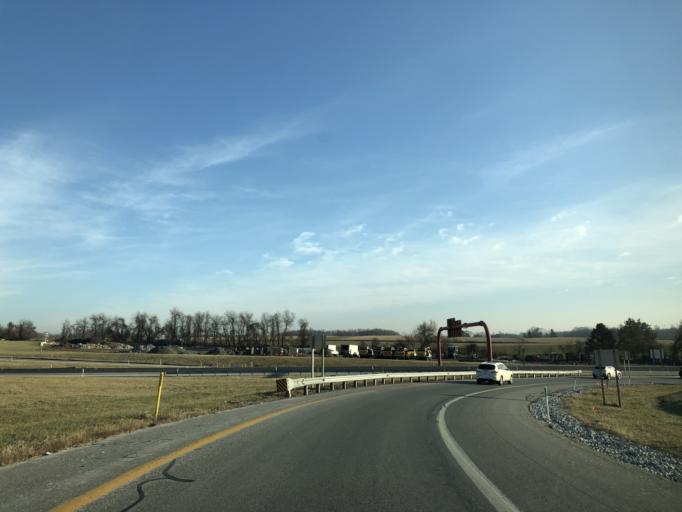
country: US
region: Pennsylvania
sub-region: Chester County
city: Chester Springs
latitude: 40.0679
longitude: -75.6684
